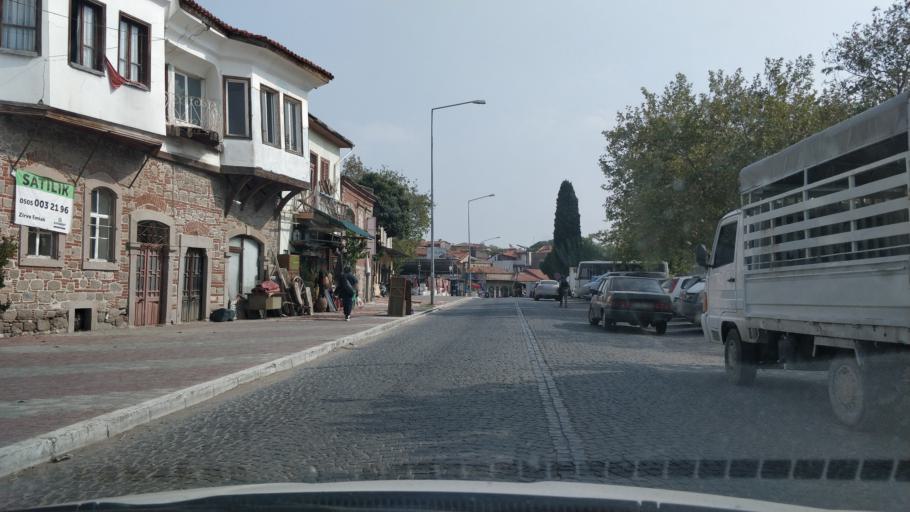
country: TR
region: Izmir
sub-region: Bergama
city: Bergama
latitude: 39.1225
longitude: 27.1827
